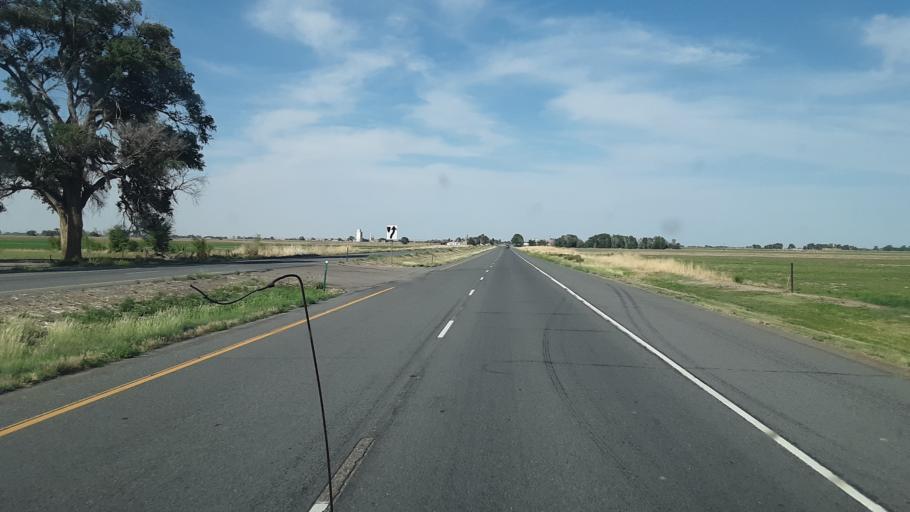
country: US
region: Colorado
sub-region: Bent County
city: Las Animas
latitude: 38.0908
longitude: -103.1694
